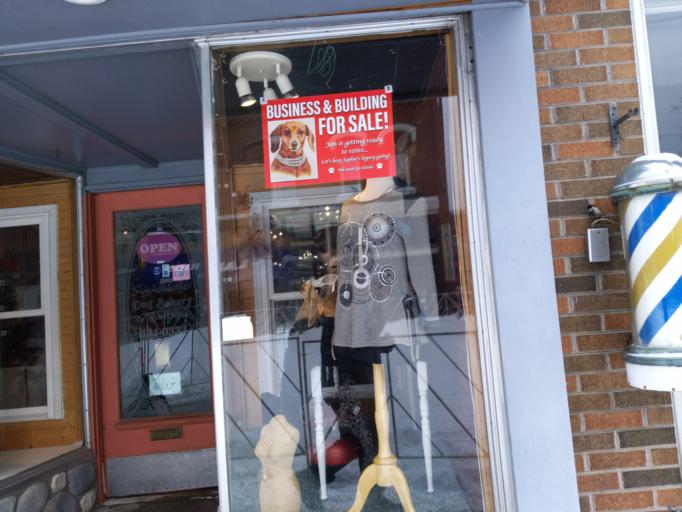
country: US
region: Wisconsin
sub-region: Sawyer County
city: Hayward
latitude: 46.0144
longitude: -91.4842
